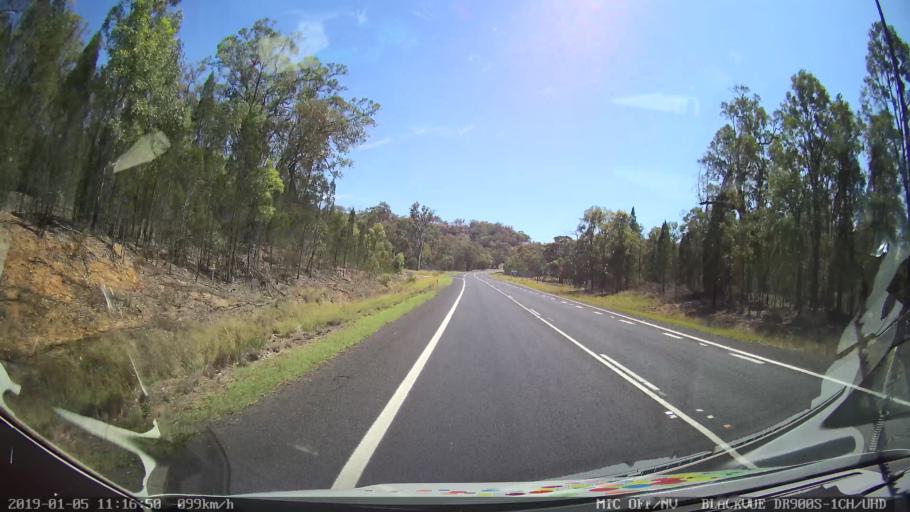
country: AU
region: New South Wales
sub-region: Warrumbungle Shire
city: Coonabarabran
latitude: -31.3336
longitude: 149.3012
